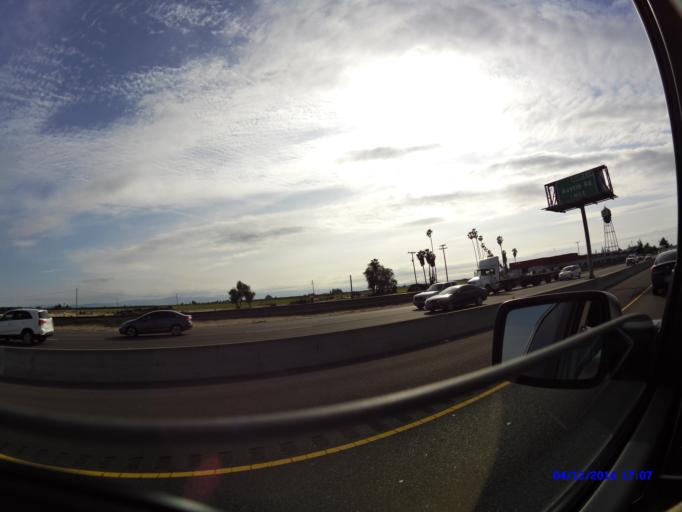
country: US
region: California
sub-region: San Joaquin County
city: Ripon
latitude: 37.7638
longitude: -121.1623
